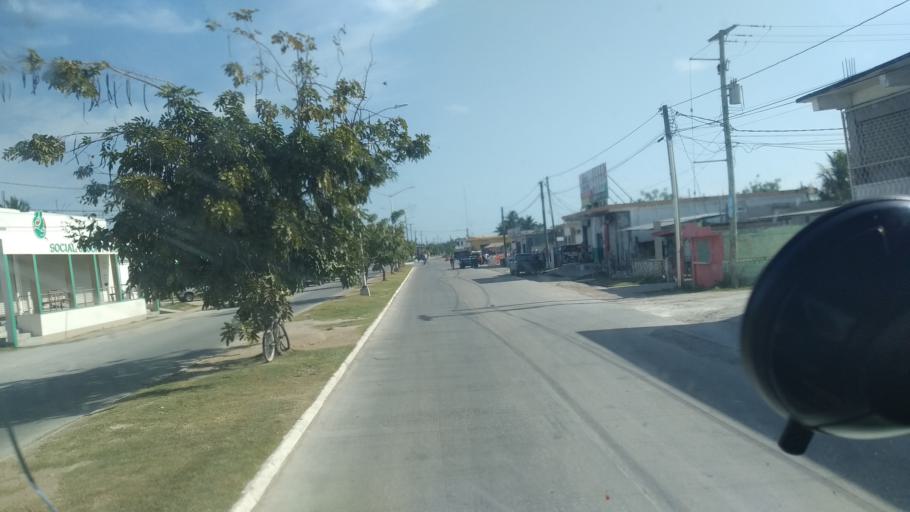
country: BZ
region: Corozal
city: Corozal
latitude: 18.3920
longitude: -88.3893
